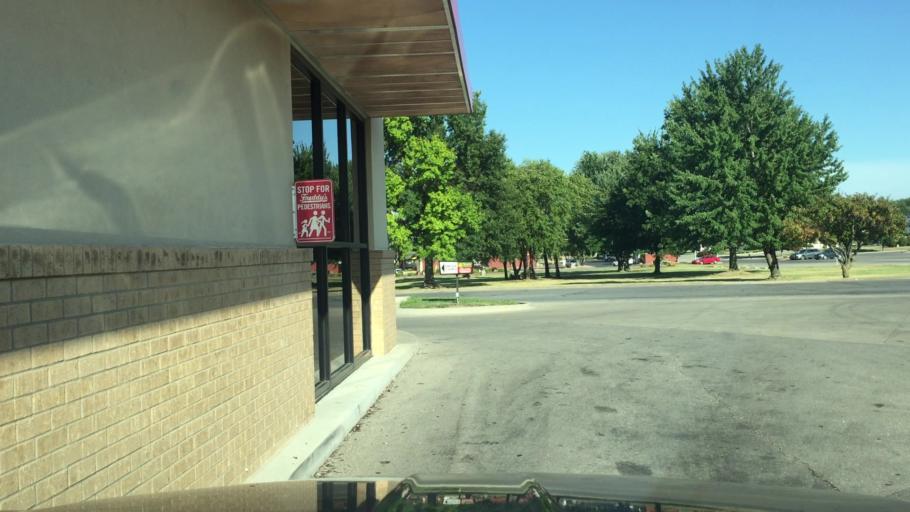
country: US
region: Missouri
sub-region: Pettis County
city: Sedalia
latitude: 38.7089
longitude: -93.2679
